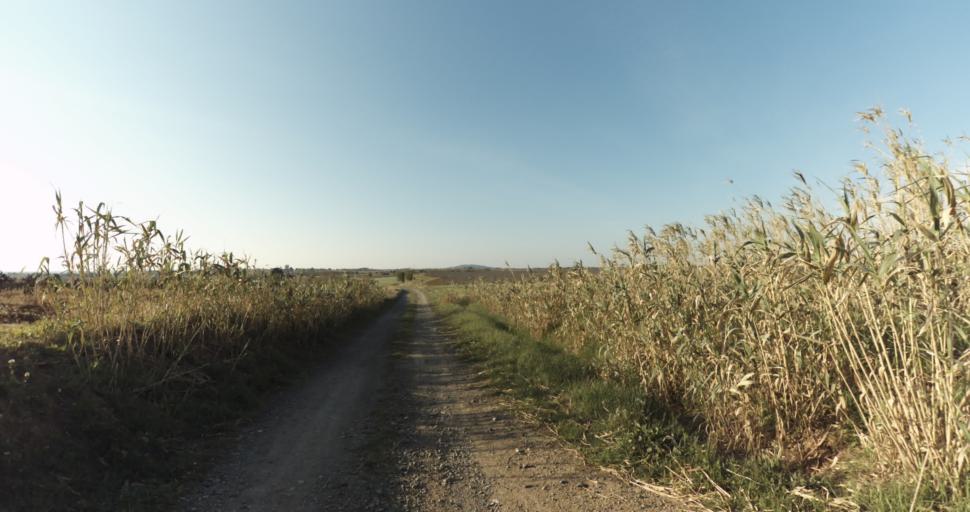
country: FR
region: Languedoc-Roussillon
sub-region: Departement de l'Herault
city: Pomerols
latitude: 43.3816
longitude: 3.5210
